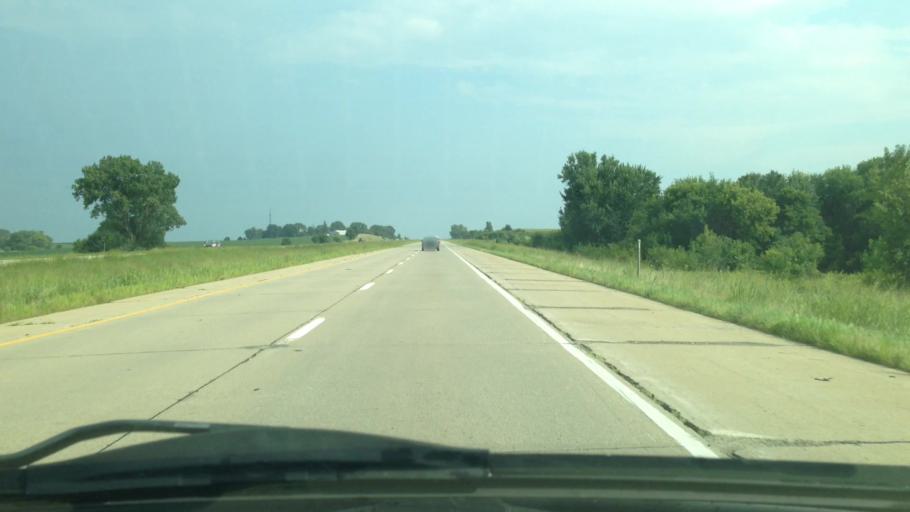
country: US
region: Iowa
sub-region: Benton County
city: Urbana
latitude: 42.2963
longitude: -91.9587
